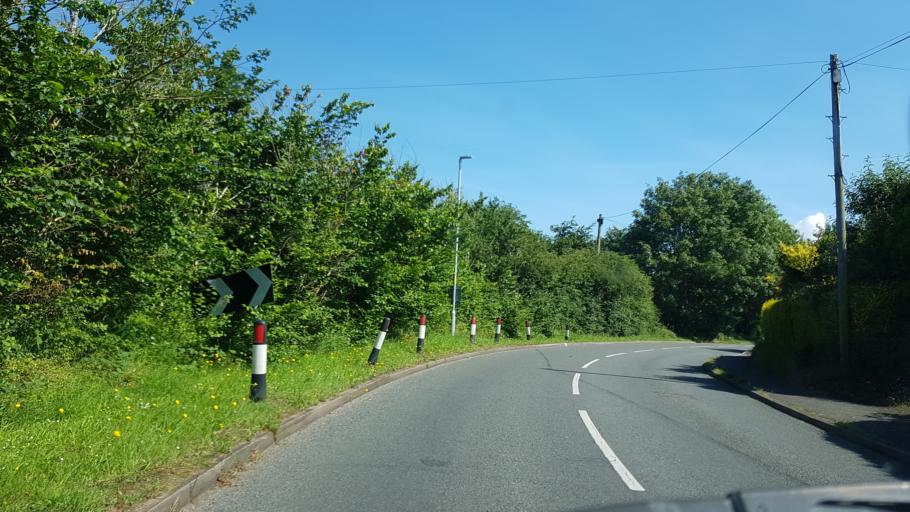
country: GB
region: England
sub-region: Worcestershire
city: Stourport-on-Severn
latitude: 52.3506
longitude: -2.2978
